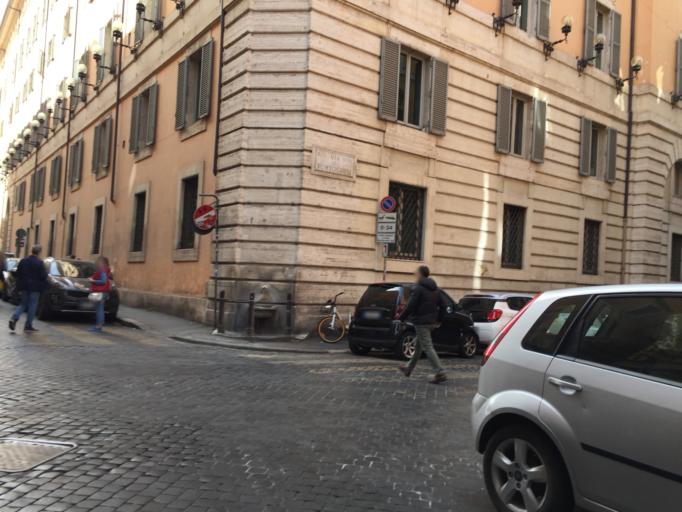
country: VA
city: Vatican City
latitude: 41.9018
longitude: 12.4752
